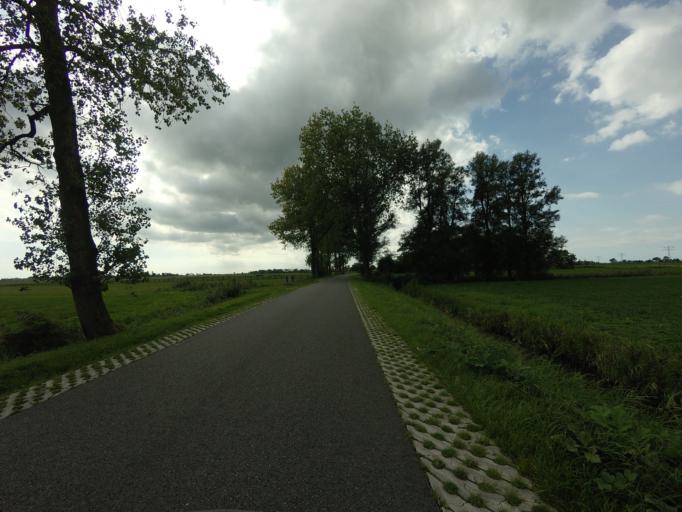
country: NL
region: Friesland
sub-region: Gemeente Littenseradiel
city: Wommels
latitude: 53.0678
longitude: 5.5774
